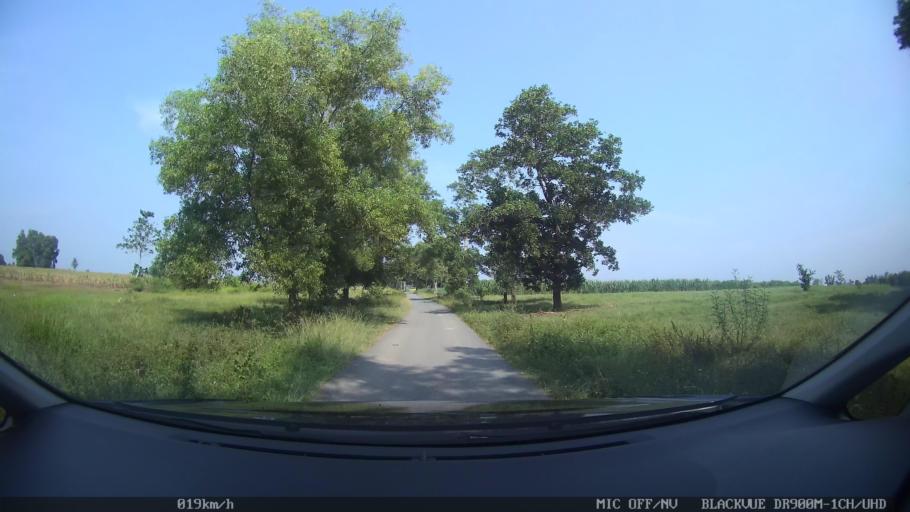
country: ID
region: Lampung
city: Natar
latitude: -5.2542
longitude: 105.2043
